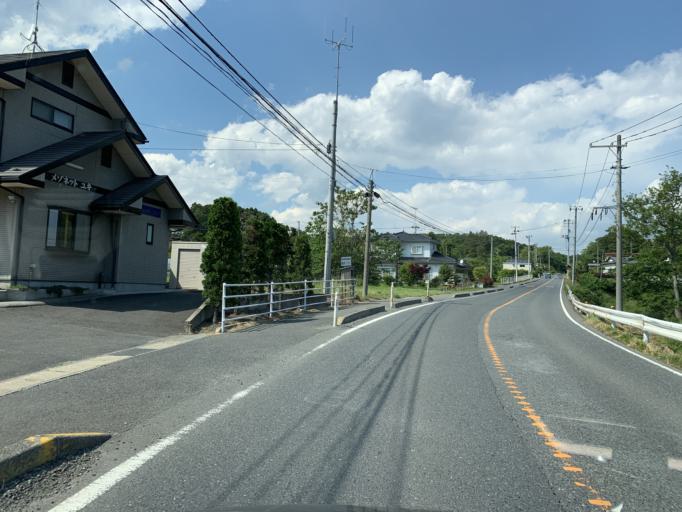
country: JP
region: Miyagi
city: Wakuya
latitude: 38.4885
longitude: 141.1076
